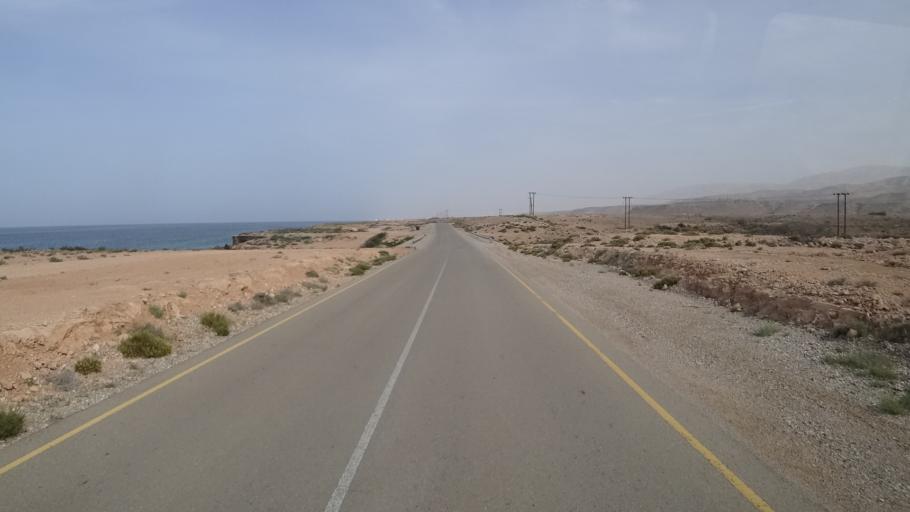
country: OM
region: Ash Sharqiyah
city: Al Qabil
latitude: 23.0128
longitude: 59.1040
